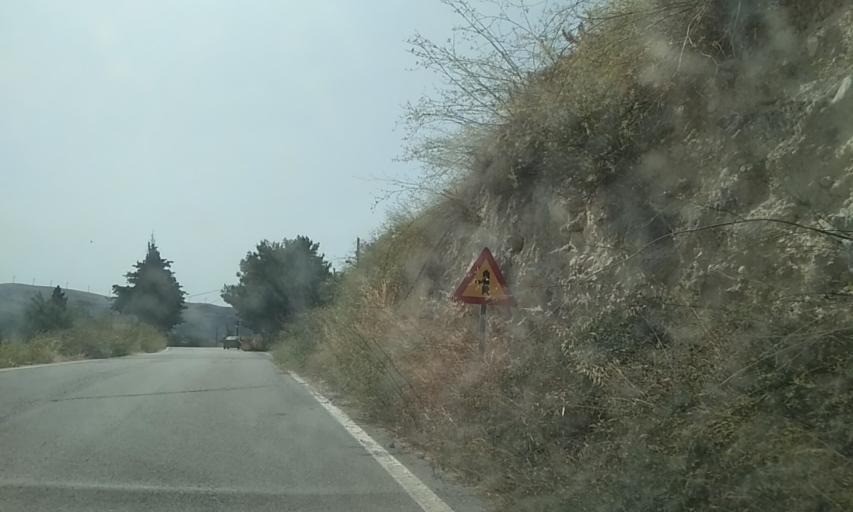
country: GR
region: Crete
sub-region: Nomos Lasithiou
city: Siteia
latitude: 35.1324
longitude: 26.0748
